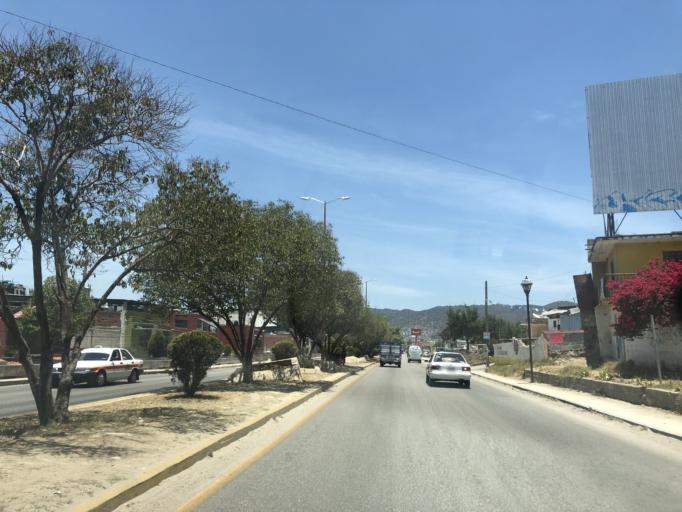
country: MX
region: Chiapas
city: San Cristobal de las Casas
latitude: 16.7223
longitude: -92.6342
